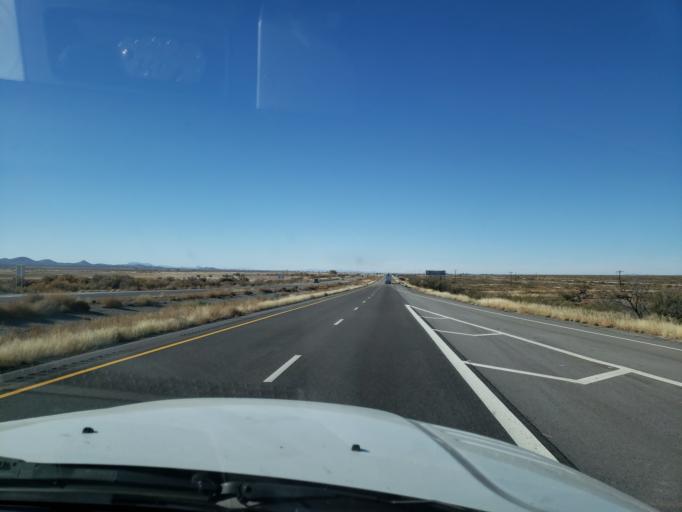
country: US
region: New Mexico
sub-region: Hidalgo County
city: Lordsburg
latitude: 32.3135
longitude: -108.6097
